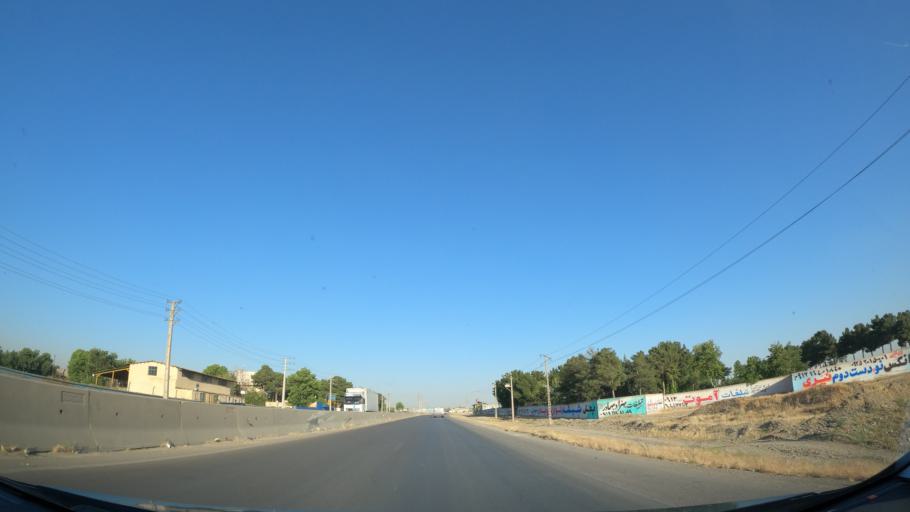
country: IR
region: Alborz
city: Hashtgerd
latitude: 35.9219
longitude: 50.7451
